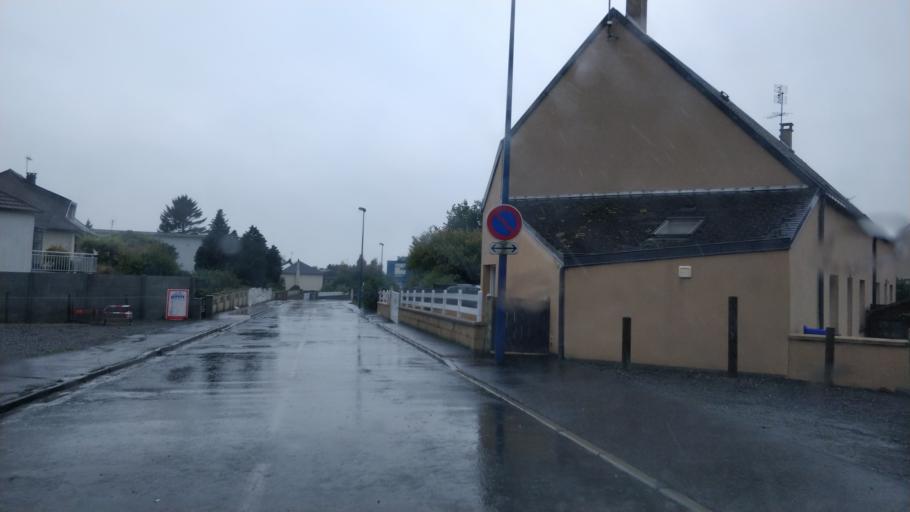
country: FR
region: Lower Normandy
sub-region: Departement de la Manche
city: Brehal
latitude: 48.8998
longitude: -1.5092
